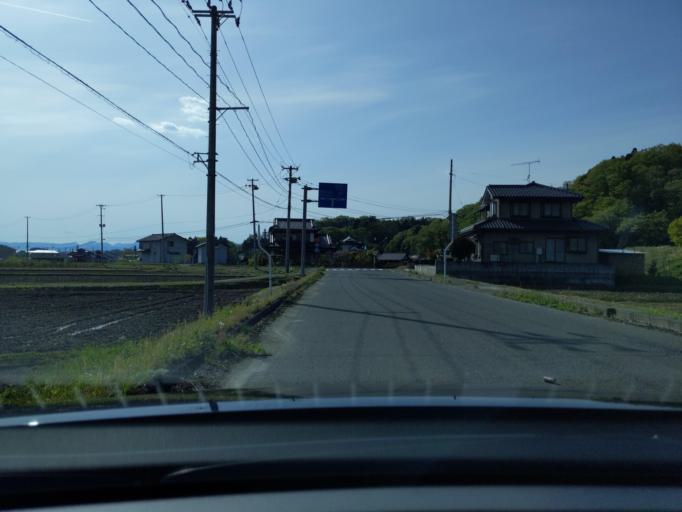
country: JP
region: Fukushima
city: Sukagawa
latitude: 37.3017
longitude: 140.3958
